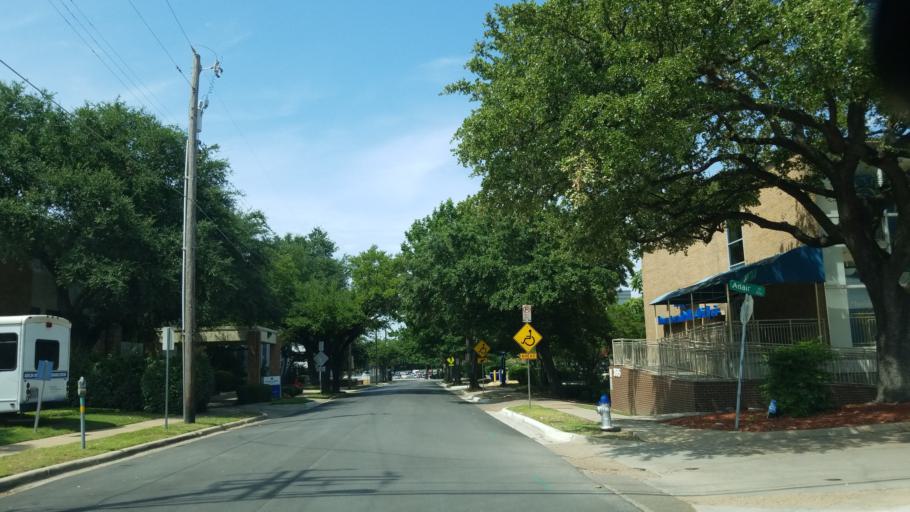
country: US
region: Texas
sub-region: Dallas County
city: Dallas
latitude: 32.7924
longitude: -96.7815
